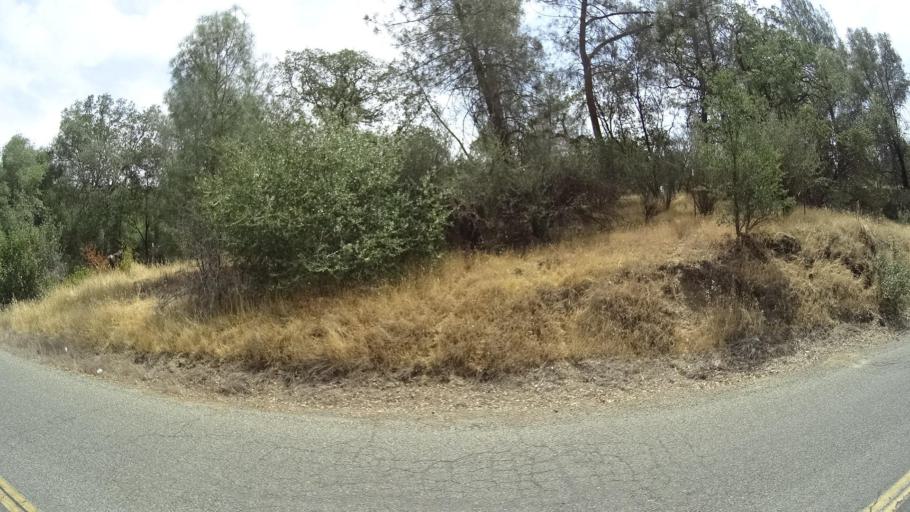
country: US
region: California
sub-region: Mariposa County
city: Mariposa
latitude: 37.4348
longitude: -119.8575
